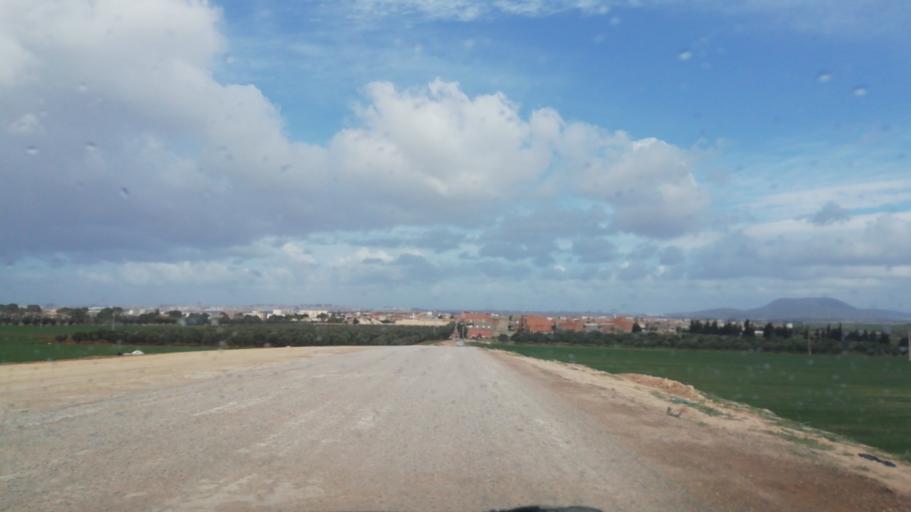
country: DZ
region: Oran
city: Sidi ech Chahmi
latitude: 35.6485
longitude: -0.5179
